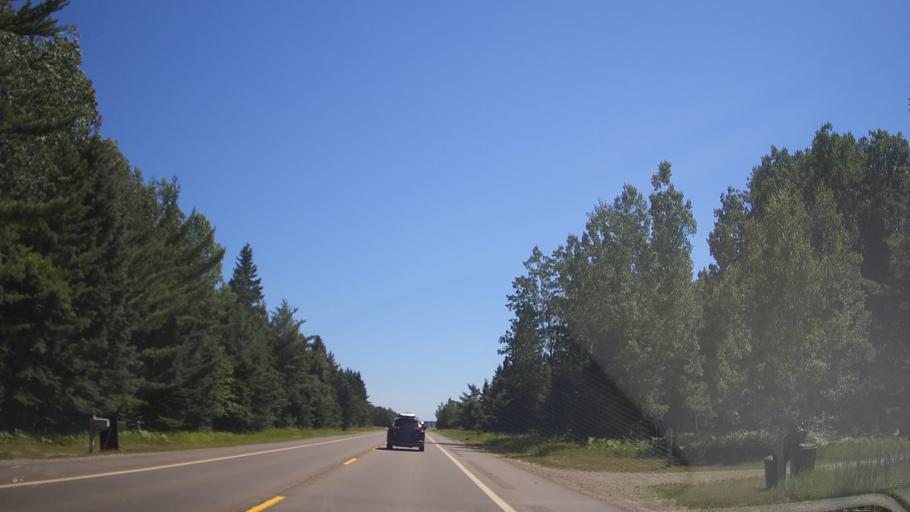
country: US
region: Michigan
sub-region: Cheboygan County
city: Indian River
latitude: 45.5856
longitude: -84.7831
